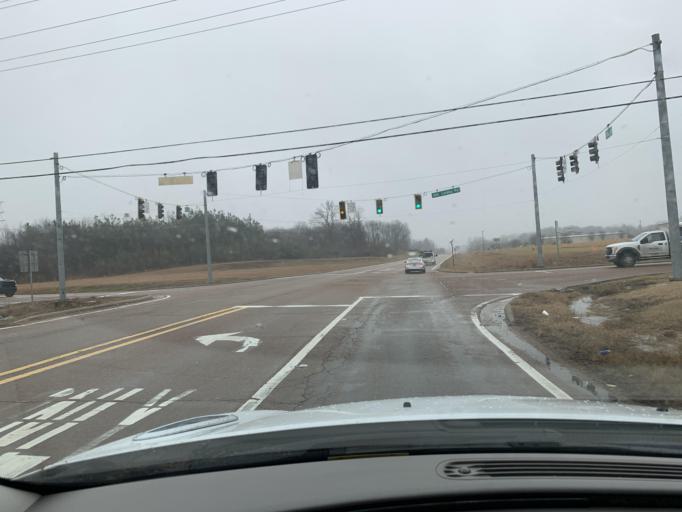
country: US
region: Mississippi
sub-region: De Soto County
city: Horn Lake
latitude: 34.9048
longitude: -89.9975
